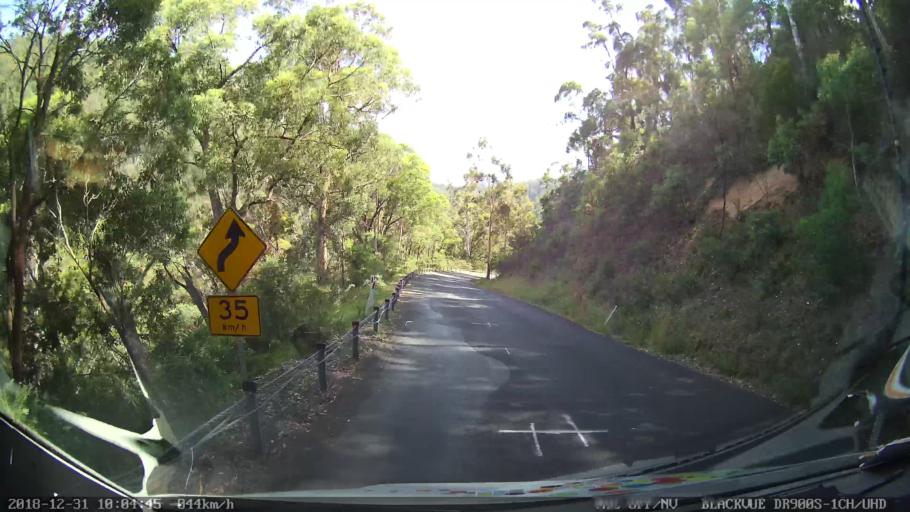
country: AU
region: New South Wales
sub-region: Snowy River
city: Jindabyne
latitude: -36.5298
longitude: 148.1925
